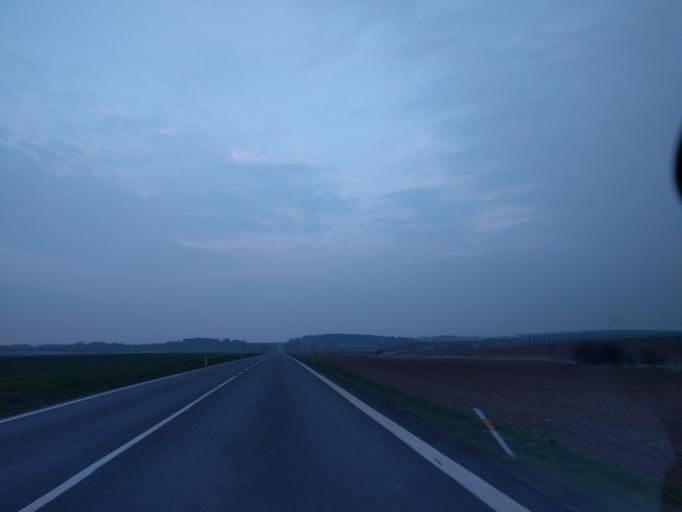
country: CZ
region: Central Bohemia
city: Rakovnik
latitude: 50.1678
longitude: 13.6480
